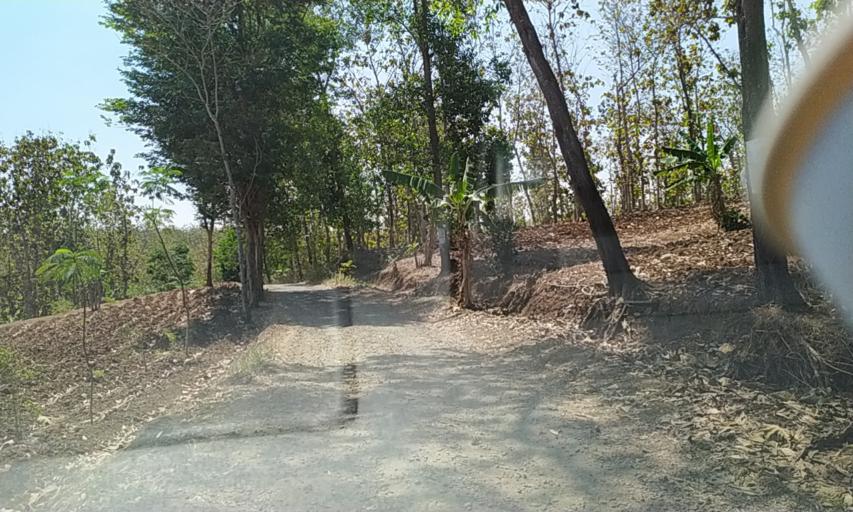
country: ID
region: Central Java
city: Prapagan
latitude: -7.5870
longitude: 108.9857
